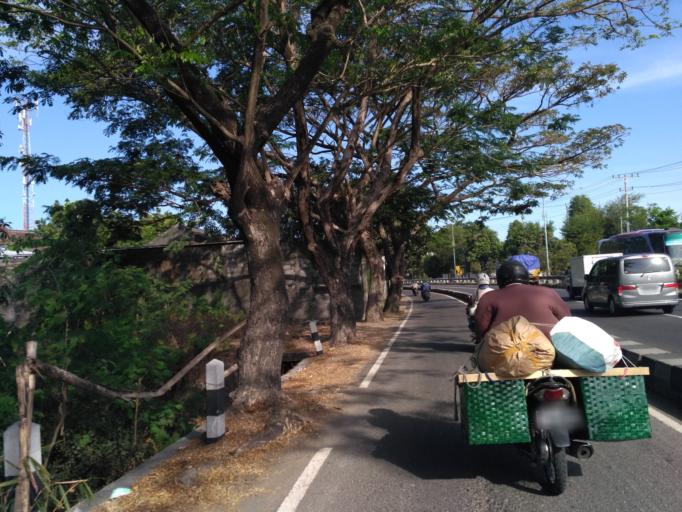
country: ID
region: Daerah Istimewa Yogyakarta
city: Sewon
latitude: -7.8349
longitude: 110.3891
